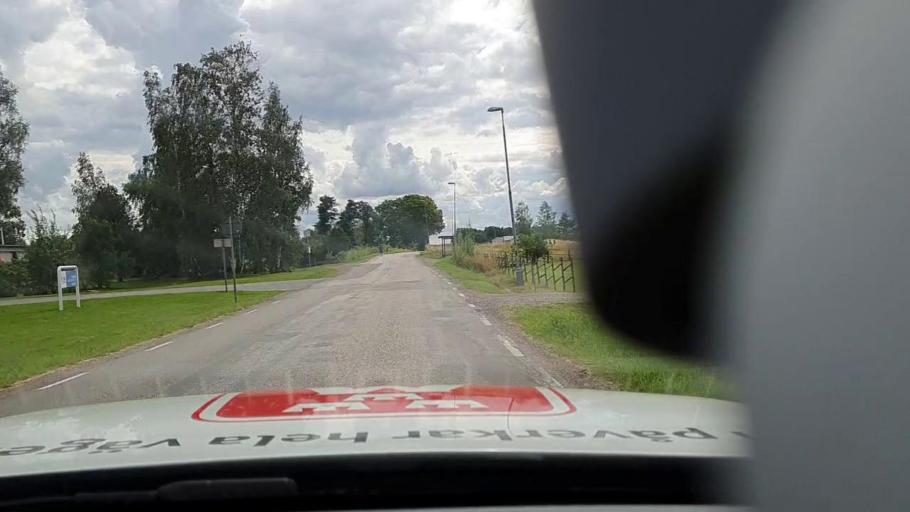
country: SE
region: Vaestra Goetaland
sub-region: Lidkopings Kommun
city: Lidkoping
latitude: 58.5589
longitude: 13.1165
